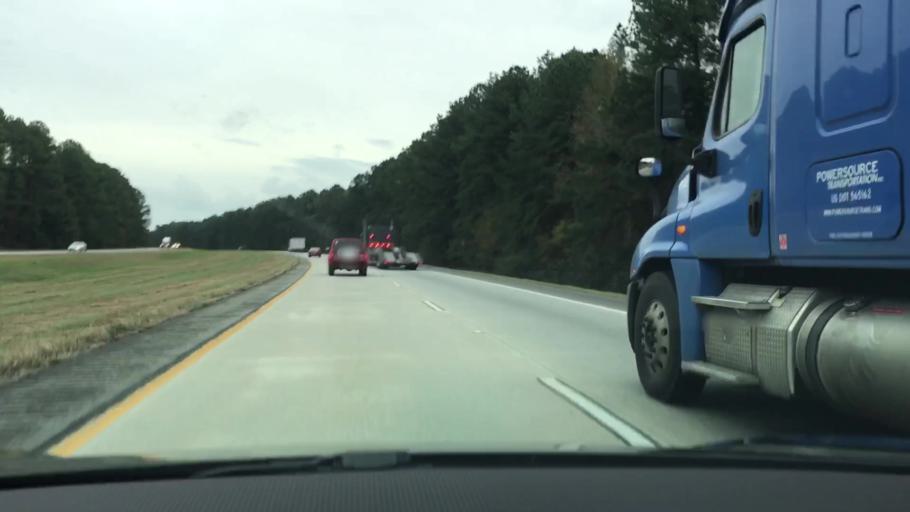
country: US
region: Georgia
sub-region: Taliaferro County
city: Crawfordville
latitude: 33.5330
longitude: -82.9894
